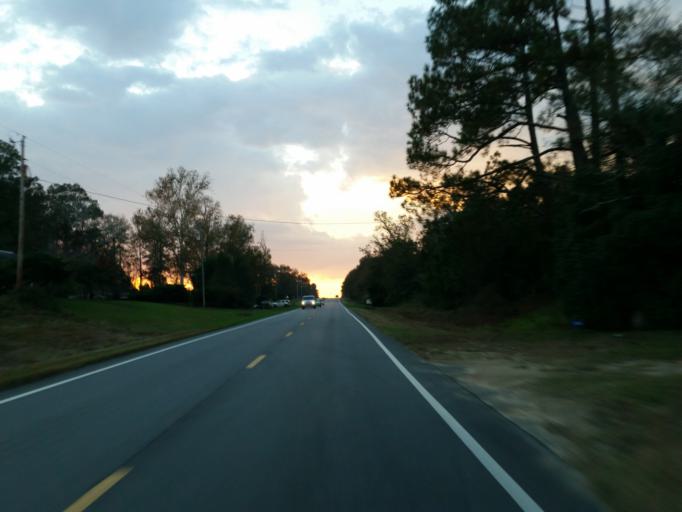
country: US
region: Georgia
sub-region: Pulaski County
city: Hawkinsville
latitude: 32.2081
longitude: -83.5516
